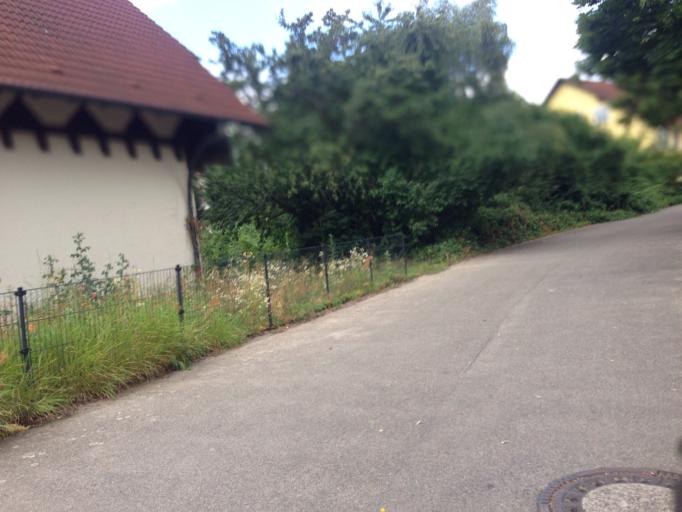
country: DE
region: Hesse
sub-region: Regierungsbezirk Darmstadt
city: Grosskrotzenburg
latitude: 50.1027
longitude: 8.9546
